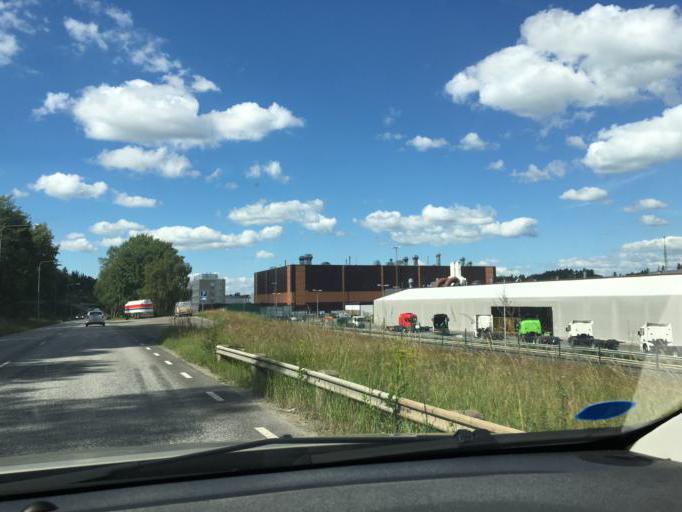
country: SE
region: Stockholm
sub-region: Sodertalje Kommun
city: Pershagen
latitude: 59.1711
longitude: 17.6371
